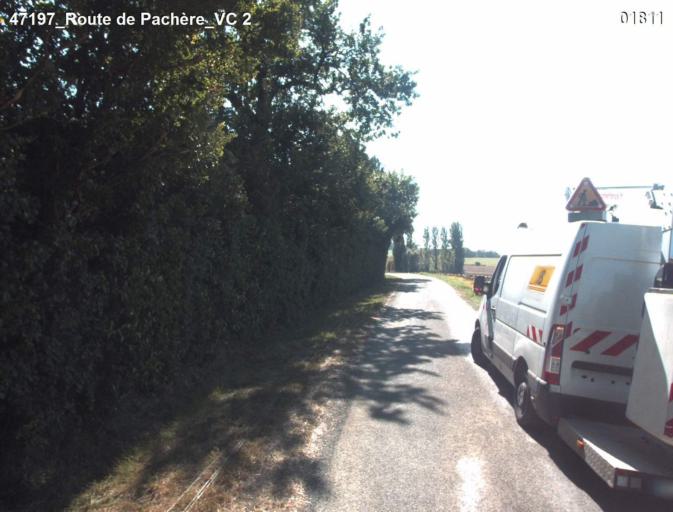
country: FR
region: Aquitaine
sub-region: Departement du Lot-et-Garonne
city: Laplume
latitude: 44.0886
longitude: 0.4526
